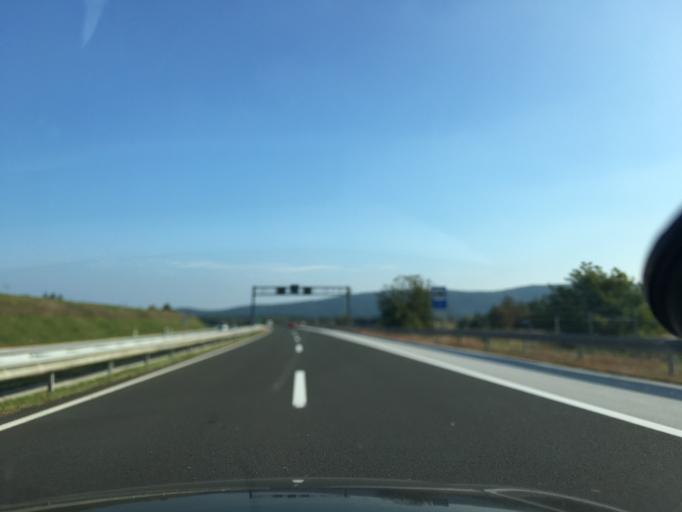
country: HR
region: Karlovacka
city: Ostarije
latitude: 45.2251
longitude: 15.2632
